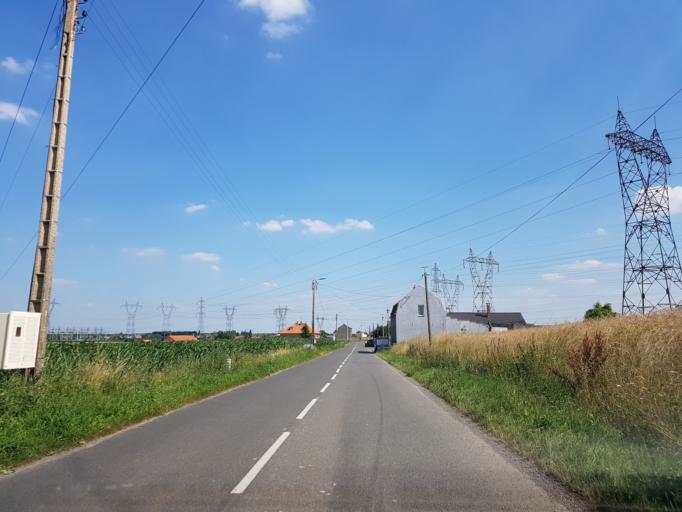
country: FR
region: Nord-Pas-de-Calais
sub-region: Departement du Nord
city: Roeulx
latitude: 50.3181
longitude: 3.3244
